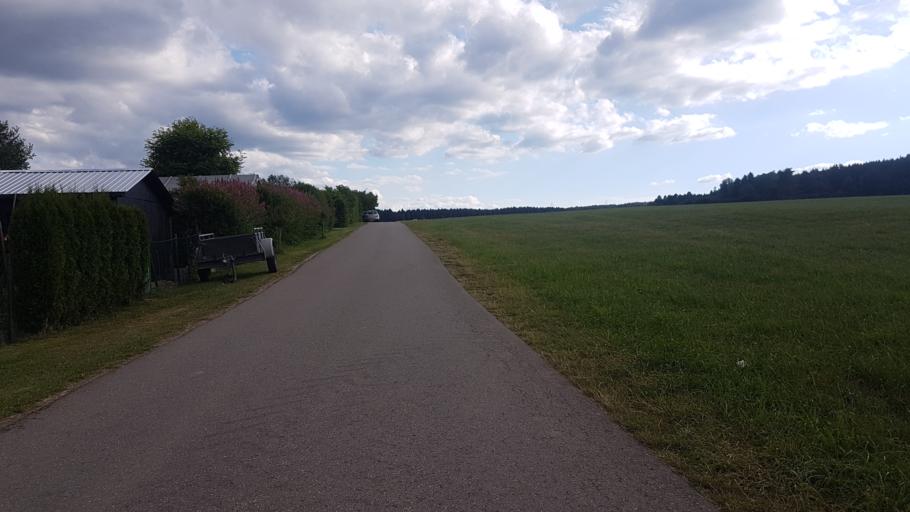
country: DE
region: Baden-Wuerttemberg
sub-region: Freiburg Region
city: Unterkirnach
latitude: 48.0342
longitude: 8.4099
